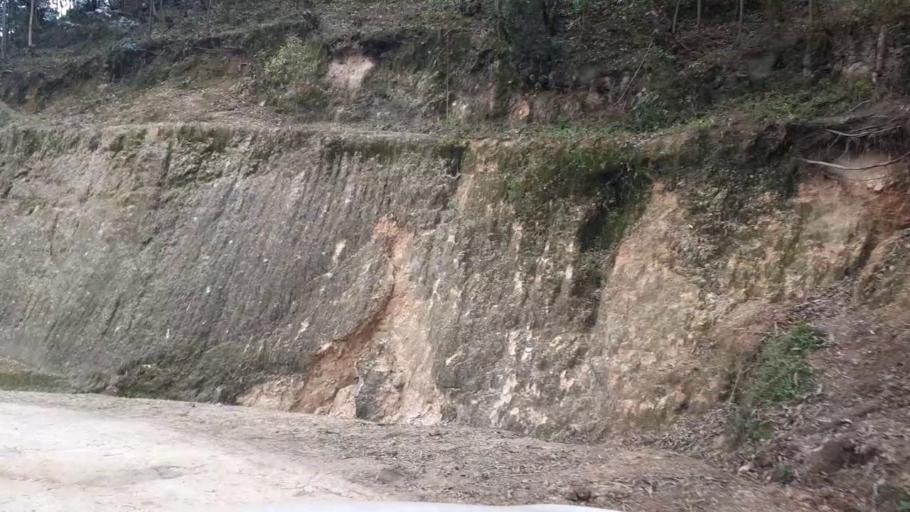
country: RW
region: Western Province
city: Kibuye
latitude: -1.8642
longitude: 29.5552
